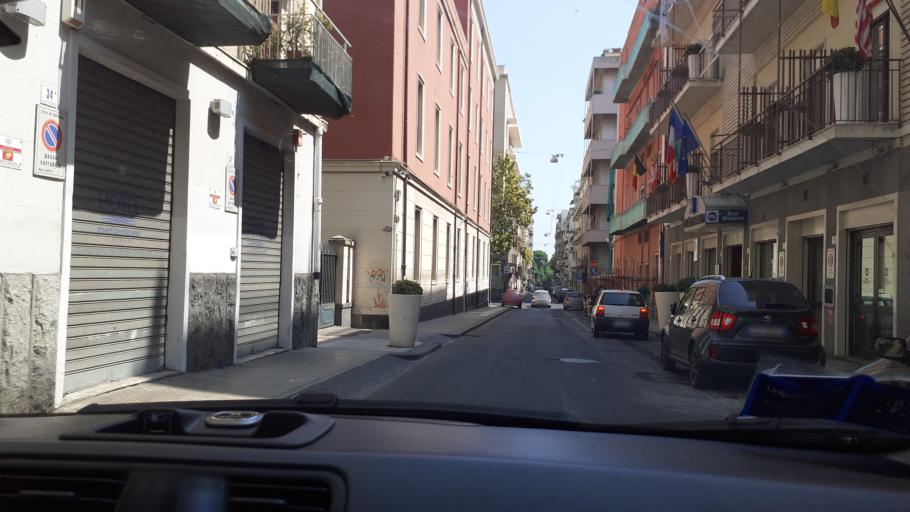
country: IT
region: Sicily
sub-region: Catania
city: Catania
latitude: 37.5098
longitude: 15.0783
